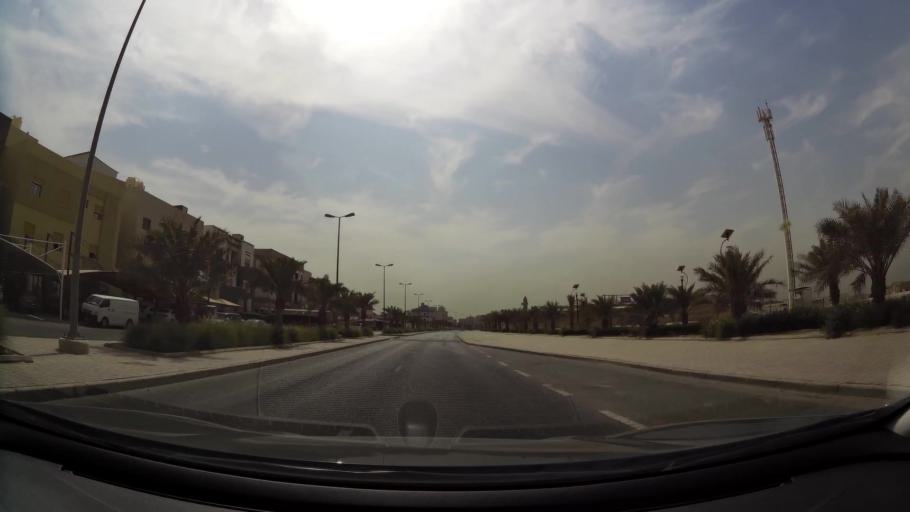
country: KW
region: Al Farwaniyah
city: Janub as Surrah
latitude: 29.2879
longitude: 48.0081
